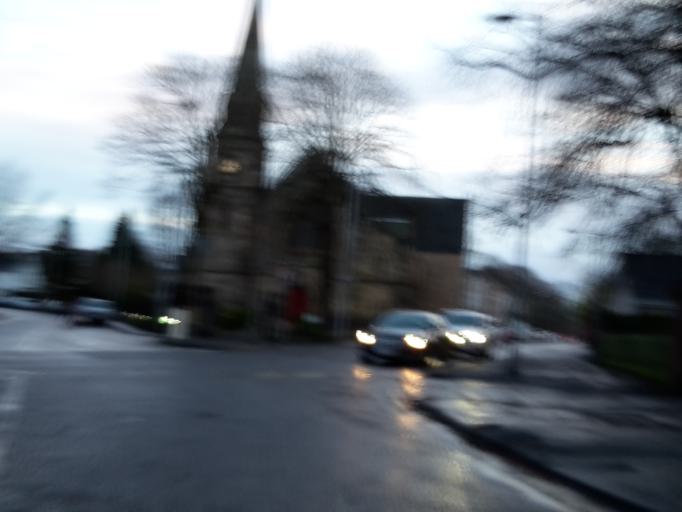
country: GB
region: Scotland
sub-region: South Lanarkshire
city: Uddingston
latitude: 55.8185
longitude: -4.0828
